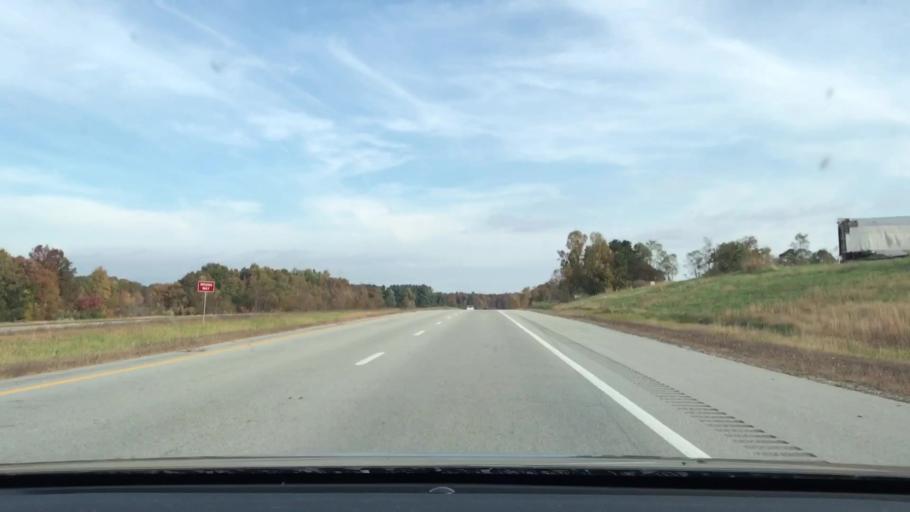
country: US
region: Tennessee
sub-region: Fentress County
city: Grimsley
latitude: 36.3214
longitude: -84.9641
